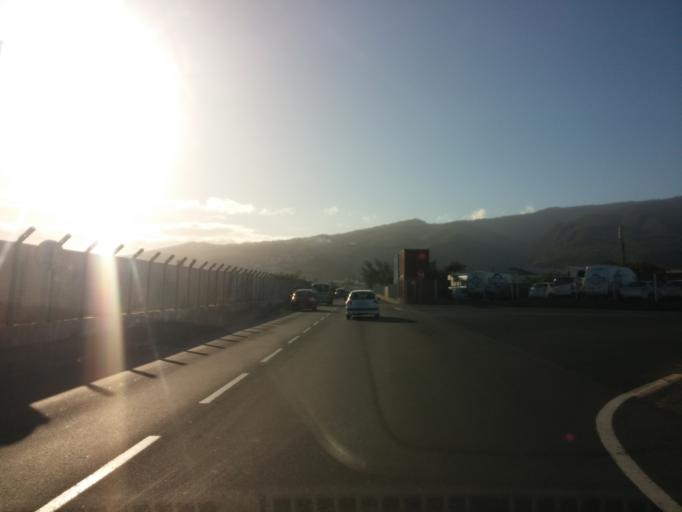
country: RE
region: Reunion
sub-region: Reunion
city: La Possession
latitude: -20.9347
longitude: 55.3169
